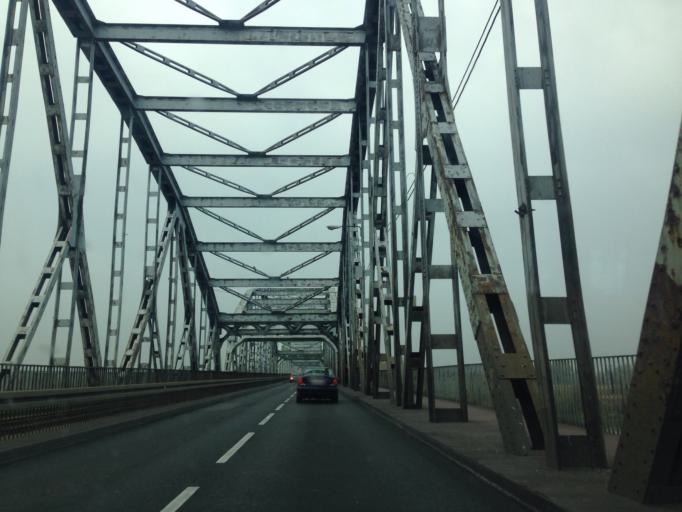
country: PL
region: Kujawsko-Pomorskie
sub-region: Grudziadz
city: Grudziadz
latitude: 53.4840
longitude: 18.7397
